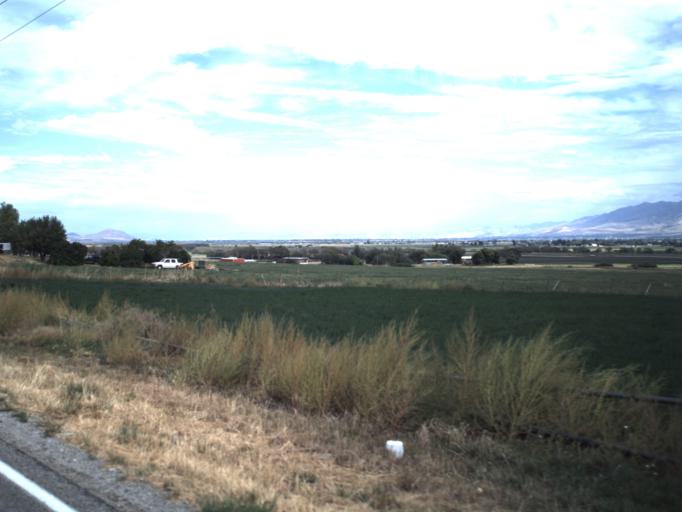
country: US
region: Utah
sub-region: Cache County
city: Wellsville
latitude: 41.6555
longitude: -111.9431
